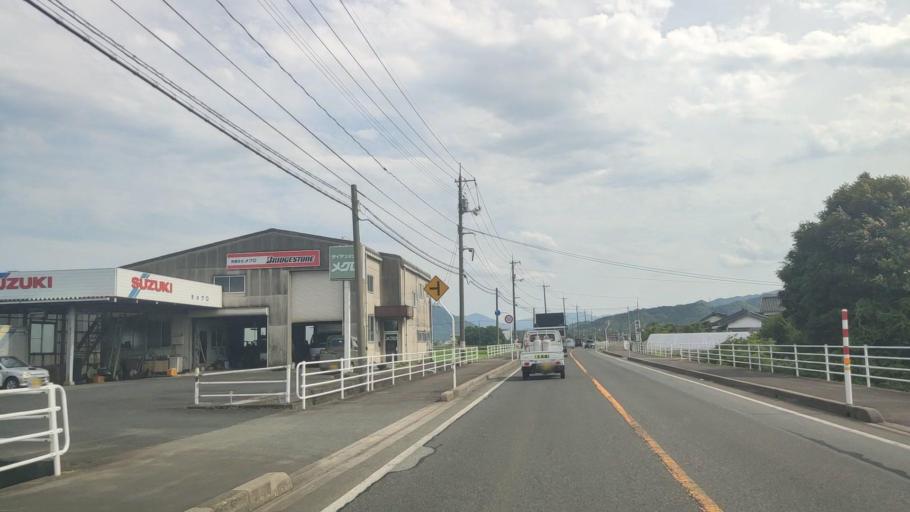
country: JP
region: Tottori
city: Tottori
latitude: 35.4611
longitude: 134.2039
